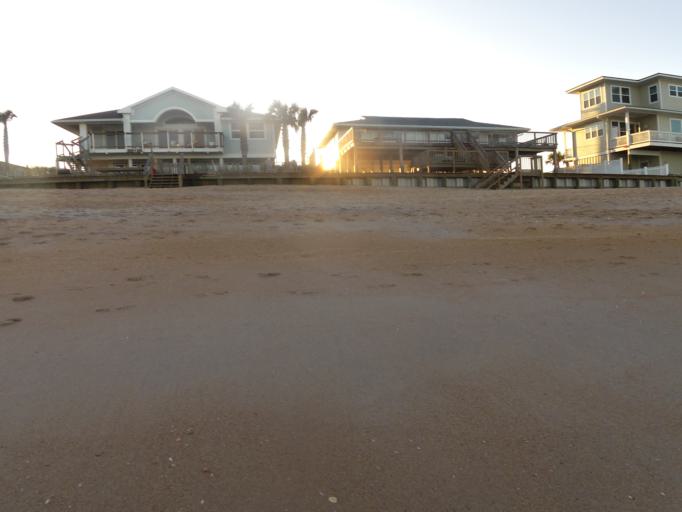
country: US
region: Florida
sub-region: Saint Johns County
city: Villano Beach
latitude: 29.9946
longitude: -81.3156
